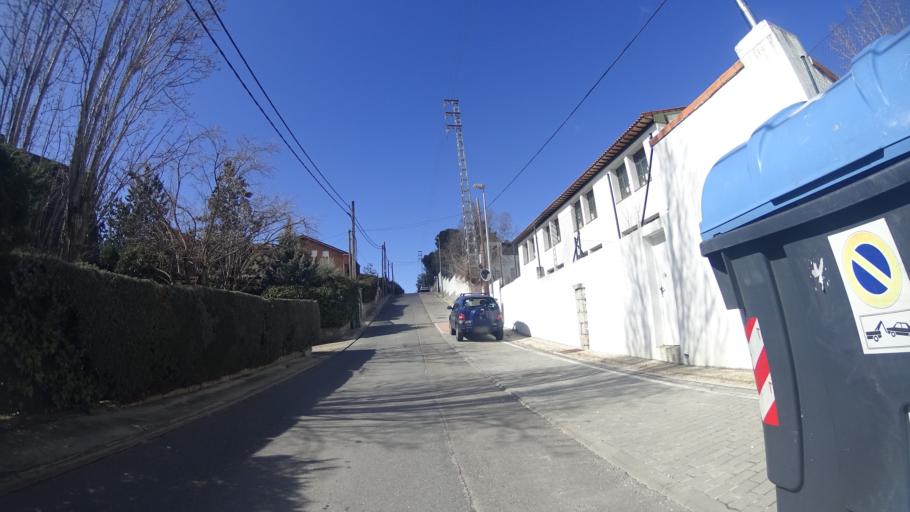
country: ES
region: Madrid
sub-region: Provincia de Madrid
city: Las Matas
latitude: 40.5638
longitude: -3.9001
